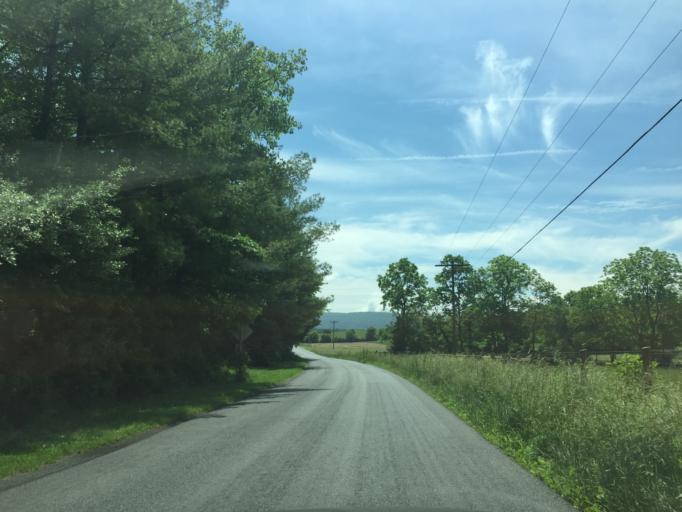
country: US
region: Virginia
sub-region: Warren County
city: Shenandoah Farms
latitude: 38.9805
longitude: -78.1297
